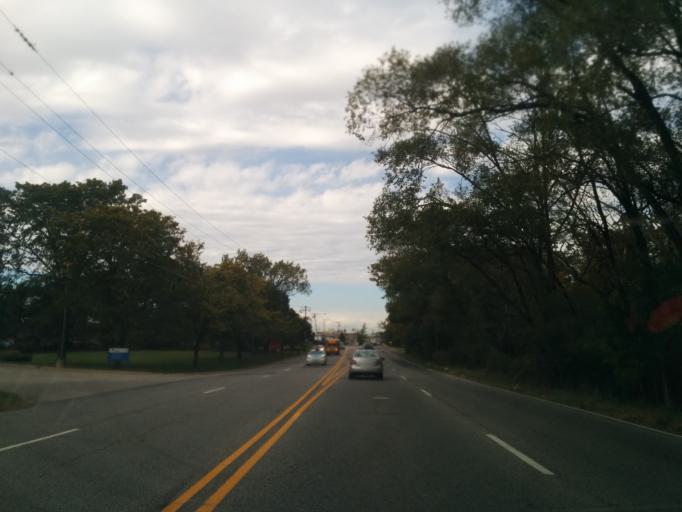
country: US
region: Illinois
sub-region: Cook County
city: Franklin Park
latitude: 41.9445
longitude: -87.8547
